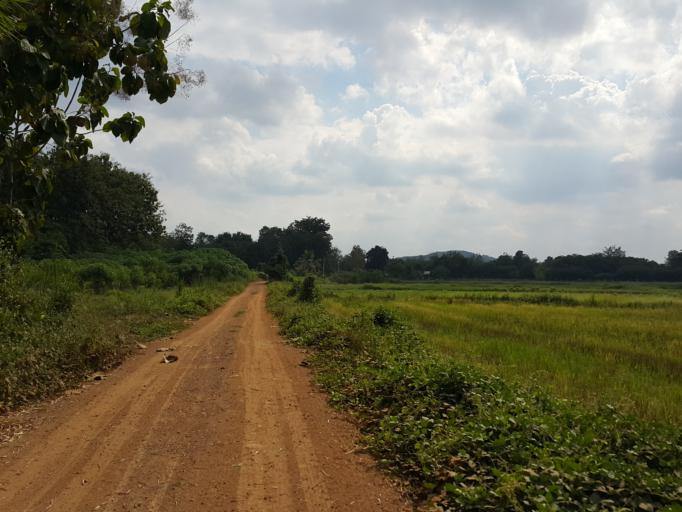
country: TH
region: Sukhothai
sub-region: Amphoe Si Satchanalai
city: Si Satchanalai
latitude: 17.4686
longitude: 99.6309
